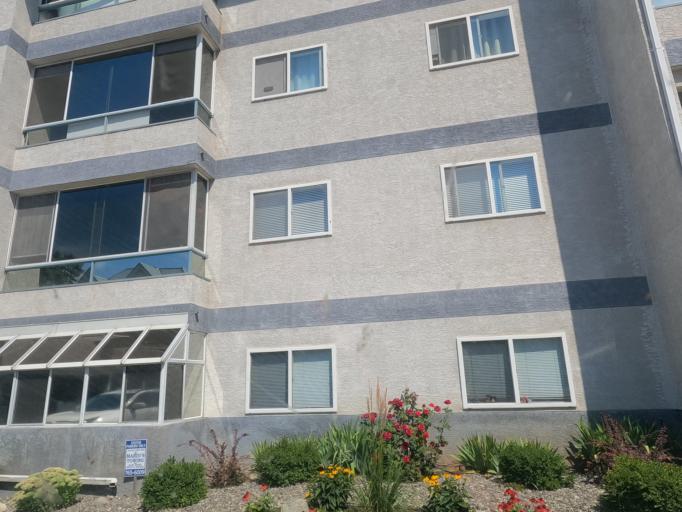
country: CA
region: British Columbia
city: Kelowna
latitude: 49.8905
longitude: -119.3999
